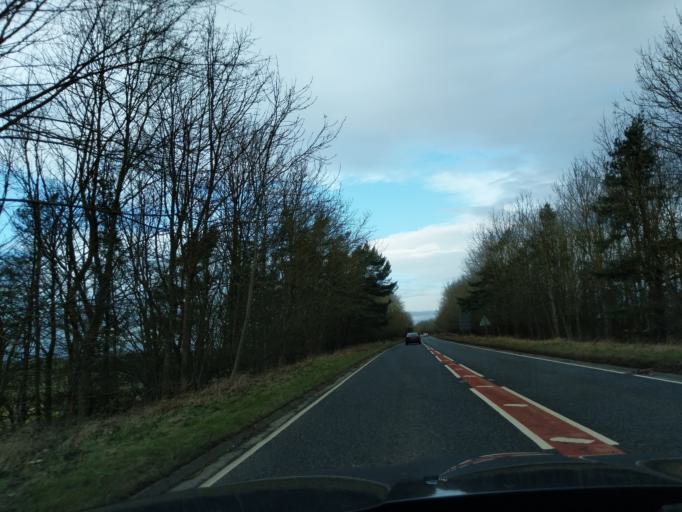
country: GB
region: England
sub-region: Northumberland
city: Meldon
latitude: 55.0857
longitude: -1.8098
